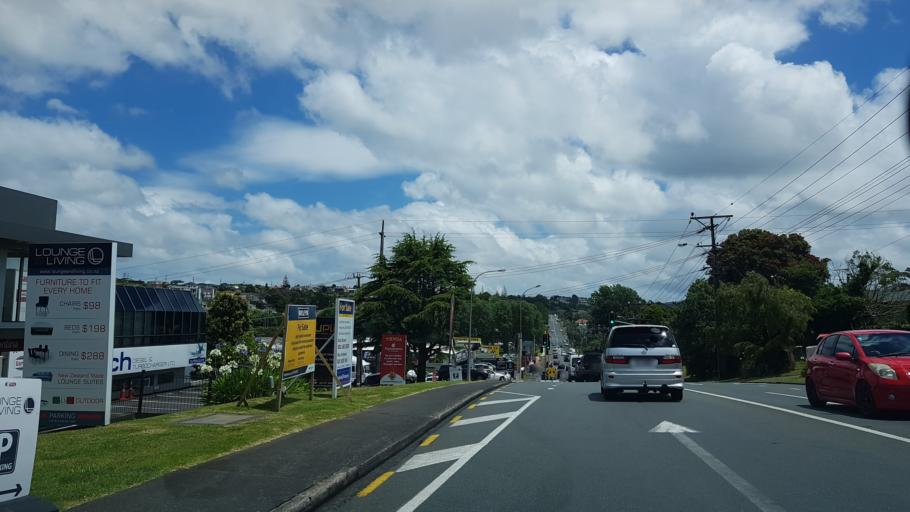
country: NZ
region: Auckland
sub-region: Auckland
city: North Shore
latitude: -36.7822
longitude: 174.7376
